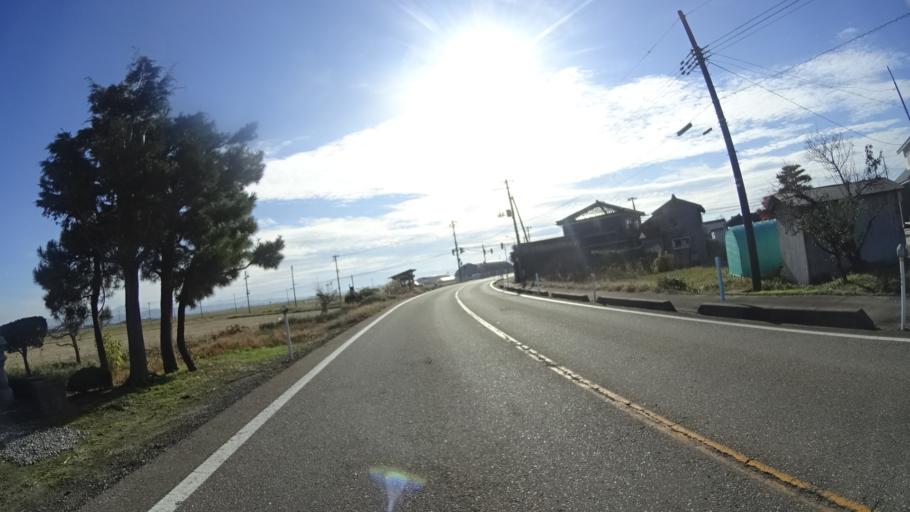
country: JP
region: Niigata
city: Mitsuke
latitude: 37.5746
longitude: 138.8406
